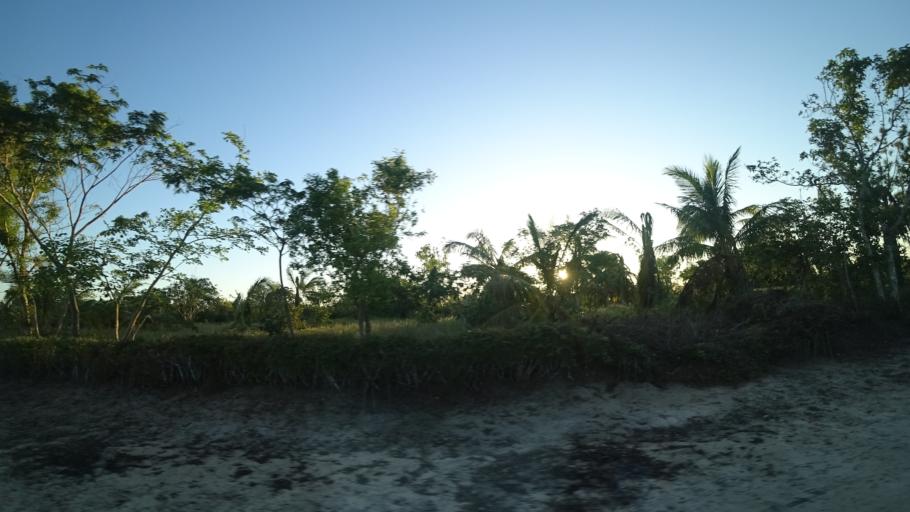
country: MZ
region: Sofala
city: Beira
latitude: -19.6411
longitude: 35.0592
